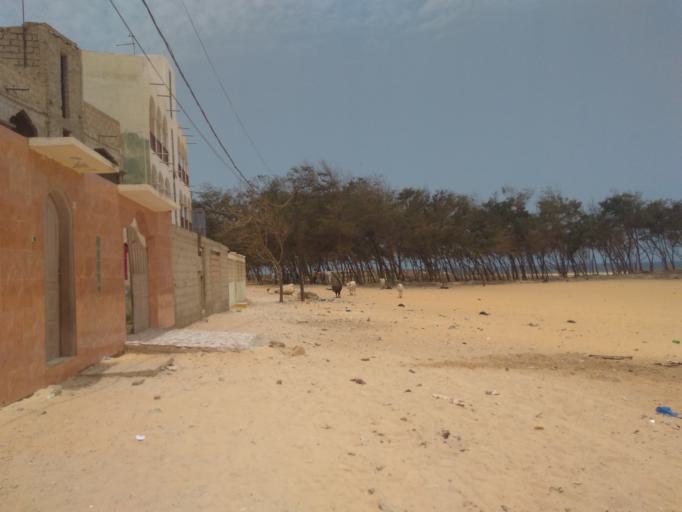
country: SN
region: Dakar
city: Pikine
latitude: 14.7889
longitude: -17.3783
